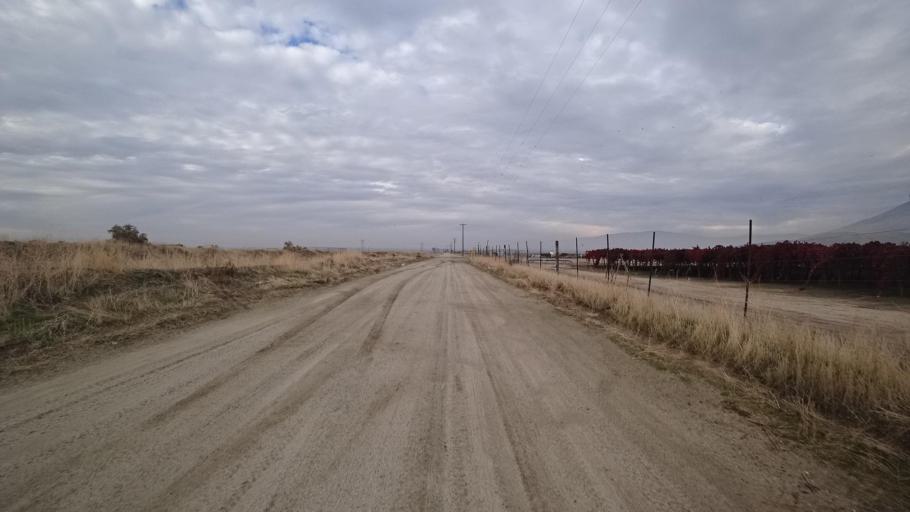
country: US
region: California
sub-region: Kern County
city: Arvin
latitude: 35.1457
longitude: -118.8146
